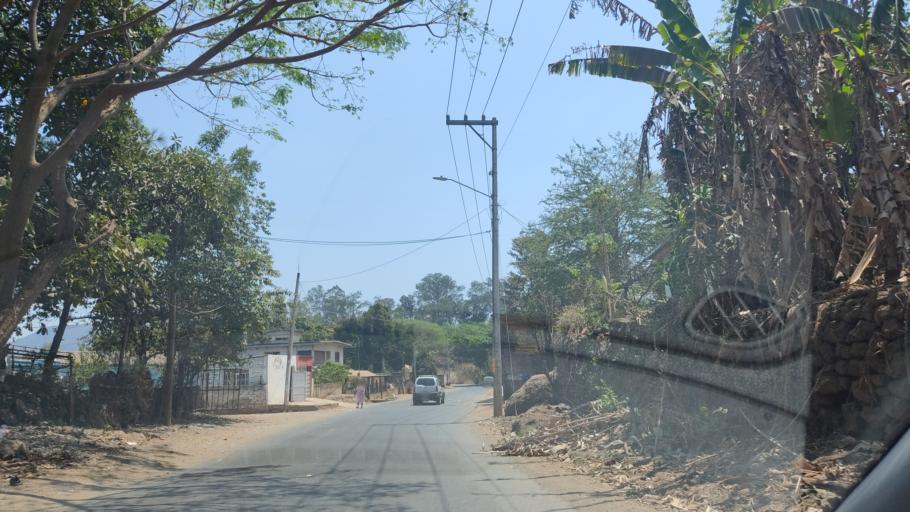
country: MX
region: Nayarit
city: Puga
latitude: 21.5859
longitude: -104.8139
